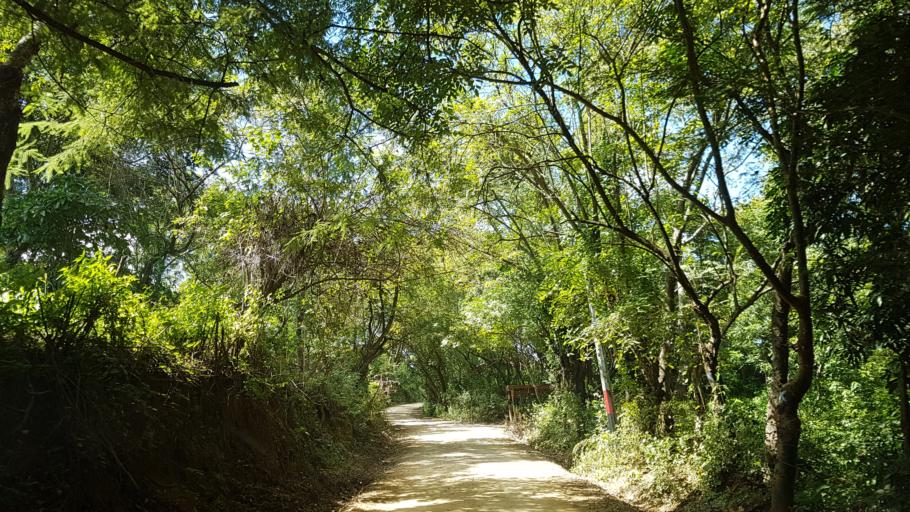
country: HN
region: El Paraiso
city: Oropoli
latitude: 13.7366
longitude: -86.6973
